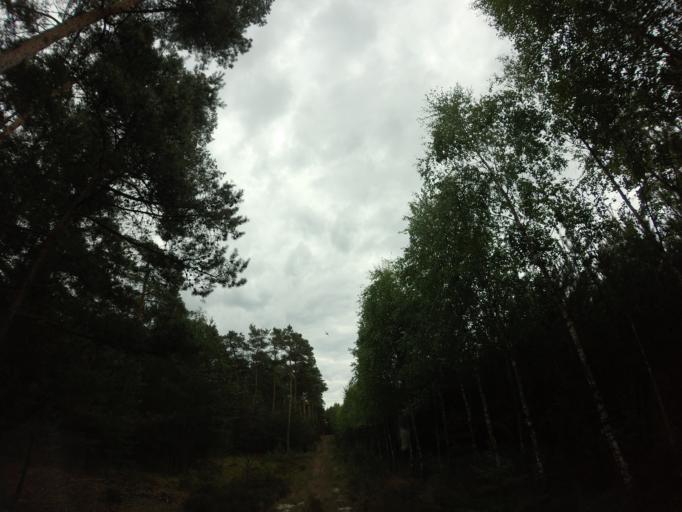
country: PL
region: West Pomeranian Voivodeship
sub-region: Powiat choszczenski
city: Drawno
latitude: 53.1600
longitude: 15.7510
